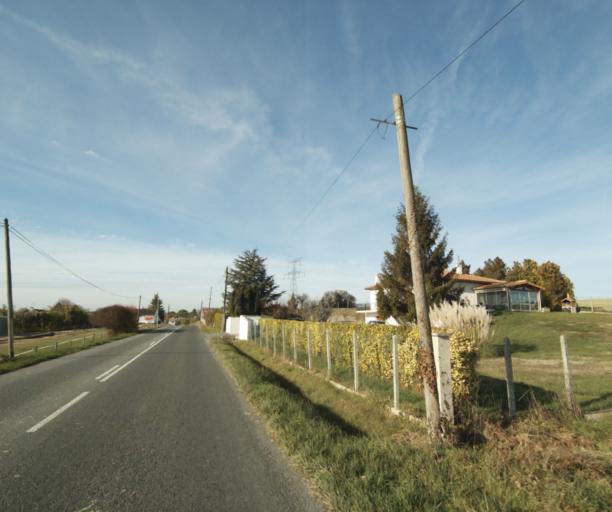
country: FR
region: Poitou-Charentes
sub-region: Departement de la Charente-Maritime
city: Chaniers
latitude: 45.7266
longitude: -0.5788
